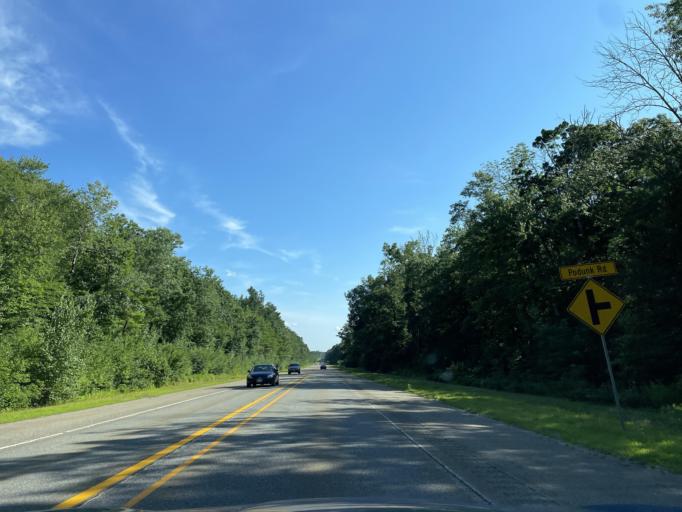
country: US
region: Massachusetts
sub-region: Worcester County
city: East Brookfield
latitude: 42.1698
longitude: -72.0317
